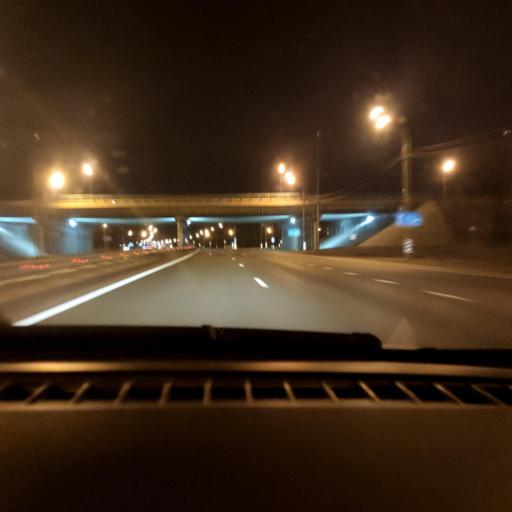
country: RU
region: Lipetsk
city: Khlevnoye
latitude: 52.2149
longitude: 39.1457
